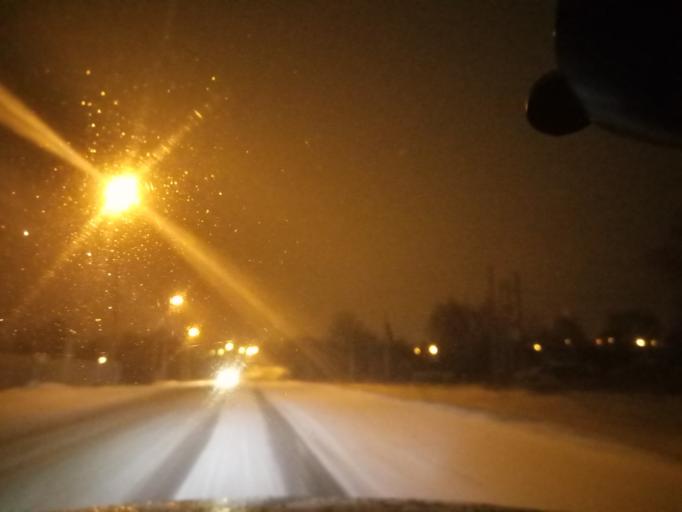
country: RU
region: Tula
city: Novomoskovsk
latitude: 53.9970
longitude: 38.2952
